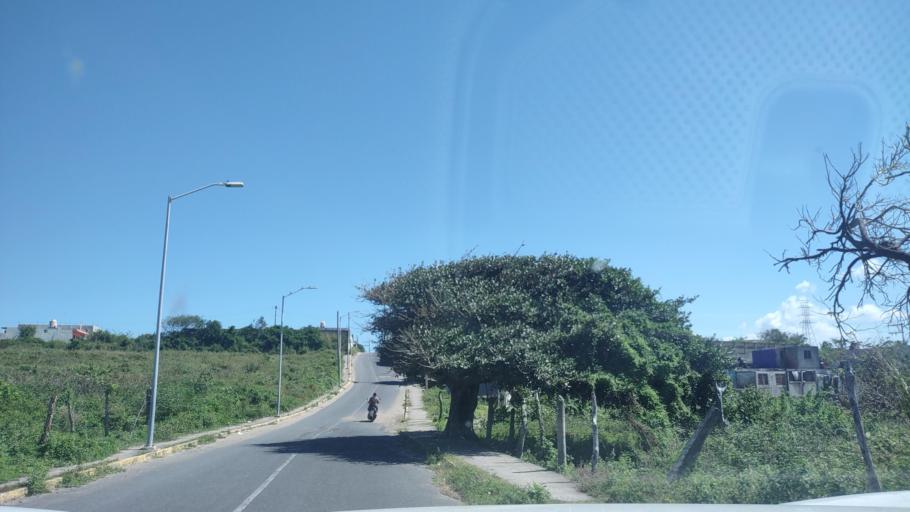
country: MX
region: Veracruz
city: Heroica Alvarado
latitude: 18.7773
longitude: -95.7605
